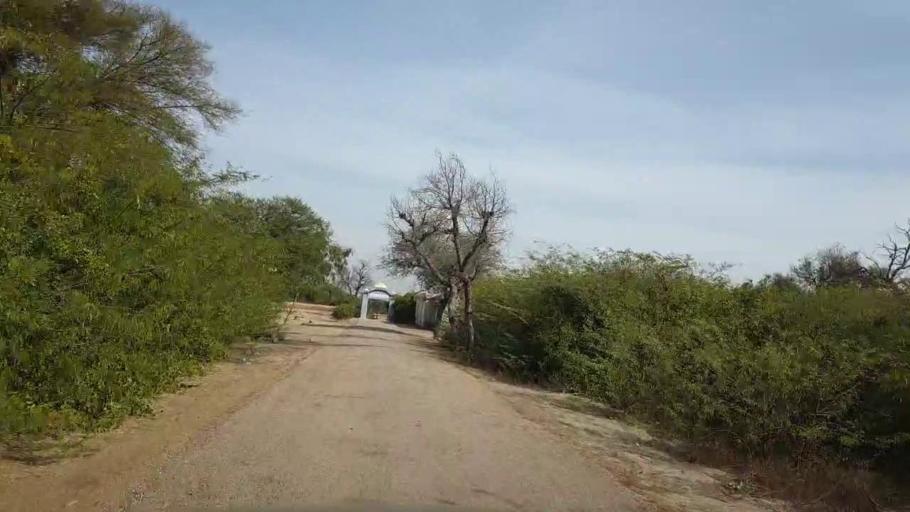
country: PK
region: Sindh
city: Kunri
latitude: 25.1579
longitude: 69.6555
